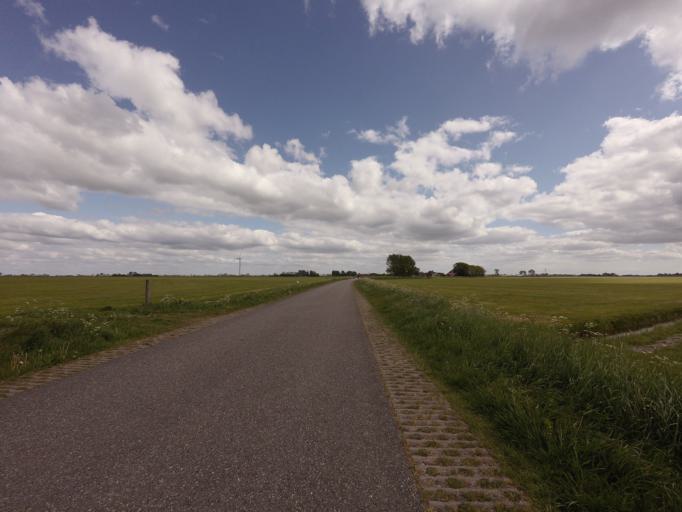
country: NL
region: Friesland
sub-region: Sudwest Fryslan
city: Bolsward
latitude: 53.0829
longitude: 5.5488
